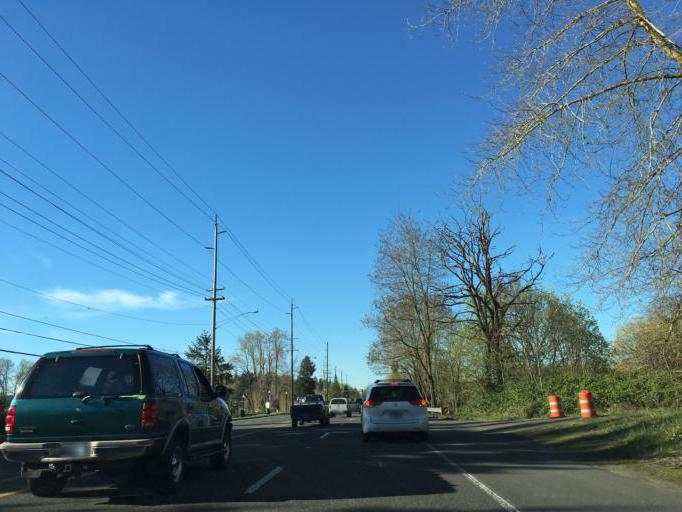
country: US
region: Oregon
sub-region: Clackamas County
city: Milwaukie
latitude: 45.4400
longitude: -122.6414
